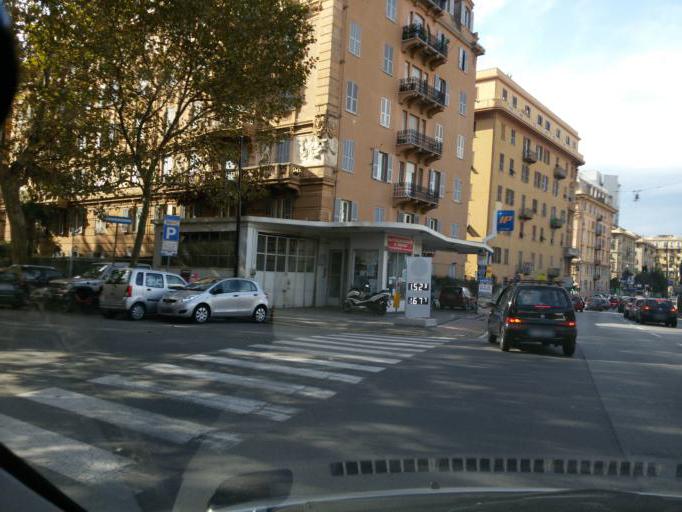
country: IT
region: Liguria
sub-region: Provincia di Genova
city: Genoa
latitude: 44.4047
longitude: 8.9535
